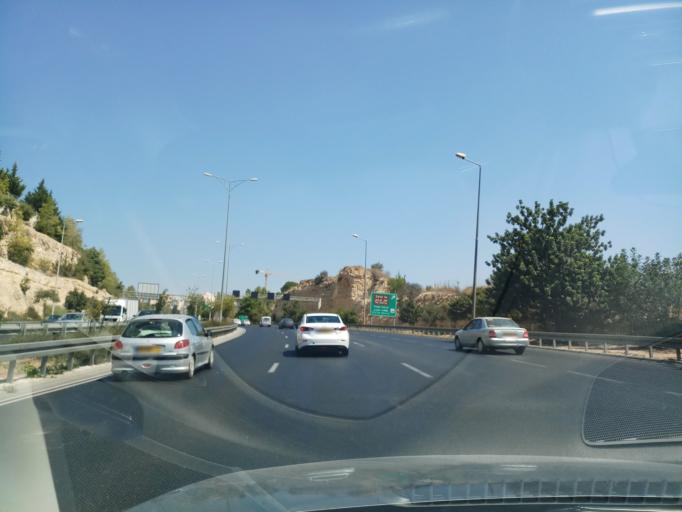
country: IL
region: Jerusalem
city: Jerusalem
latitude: 31.7609
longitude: 35.1939
